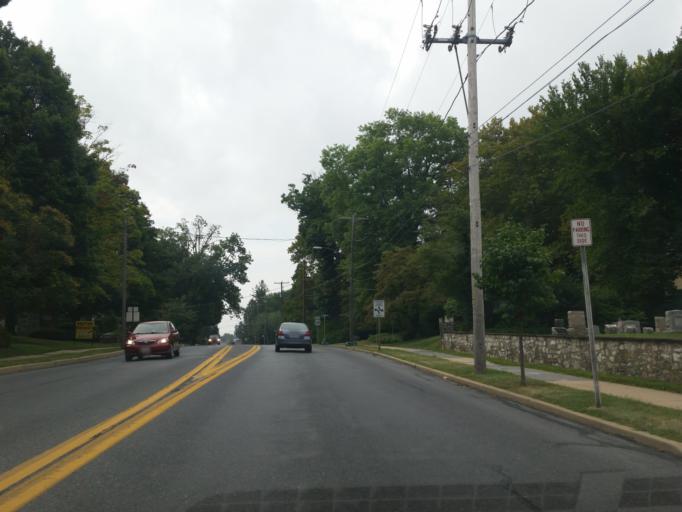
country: US
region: Pennsylvania
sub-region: Lancaster County
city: Lititz
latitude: 40.1481
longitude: -76.3064
